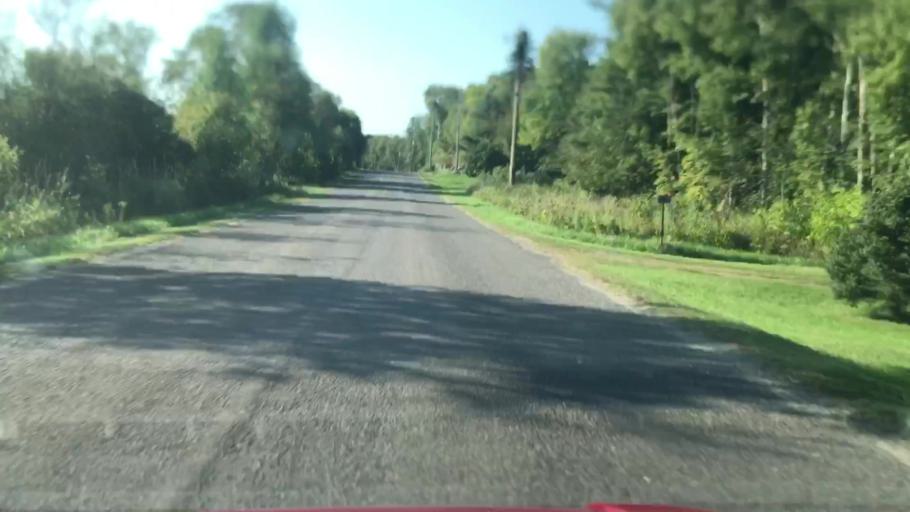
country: US
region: Michigan
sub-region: Chippewa County
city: Sault Ste. Marie
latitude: 46.2912
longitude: -84.0652
